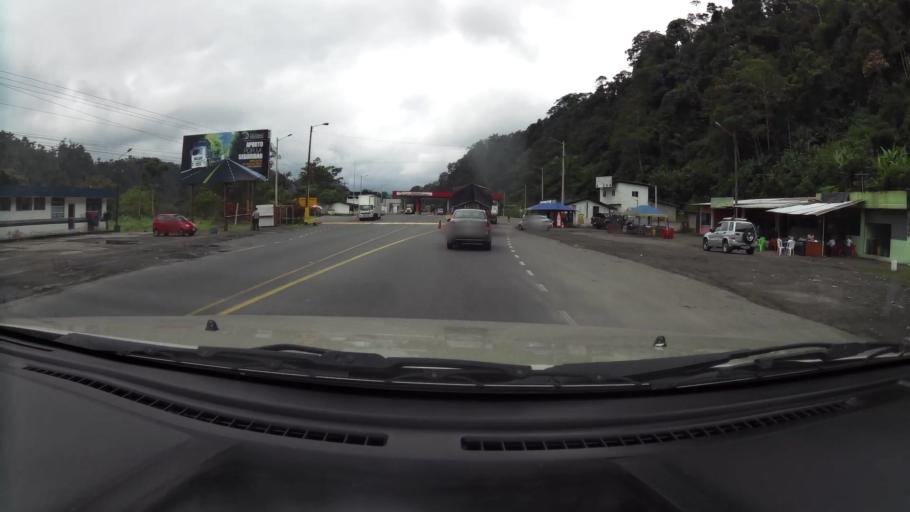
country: EC
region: Santo Domingo de los Tsachilas
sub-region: Canton Santo Domingo de los Colorados
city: Santo Domingo de los Colorados
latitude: -0.2744
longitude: -79.0790
